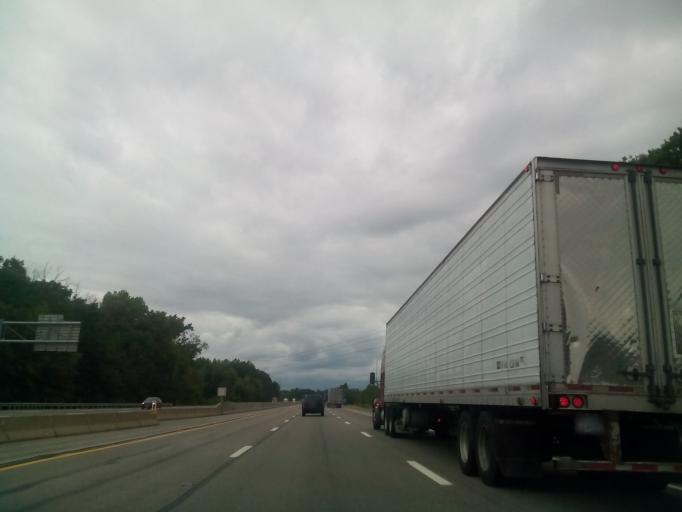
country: US
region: Ohio
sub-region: Lorain County
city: South Amherst
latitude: 41.3672
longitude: -82.2724
